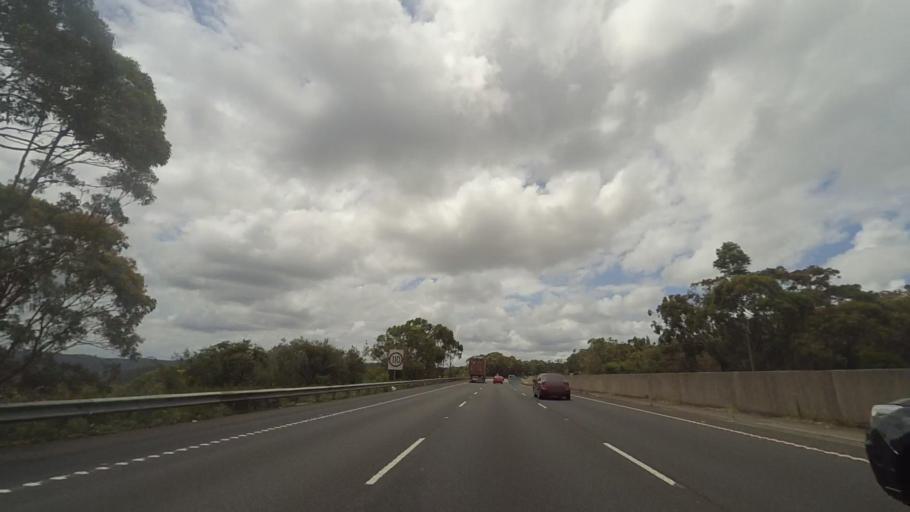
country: AU
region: New South Wales
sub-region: Gosford Shire
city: Point Clare
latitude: -33.4421
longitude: 151.2183
